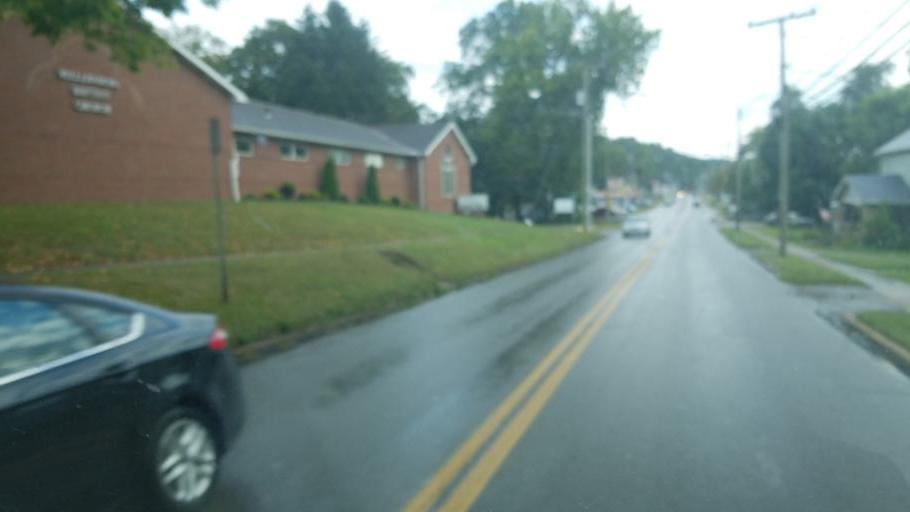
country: US
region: Ohio
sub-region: Holmes County
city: Millersburg
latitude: 40.5469
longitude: -81.9176
